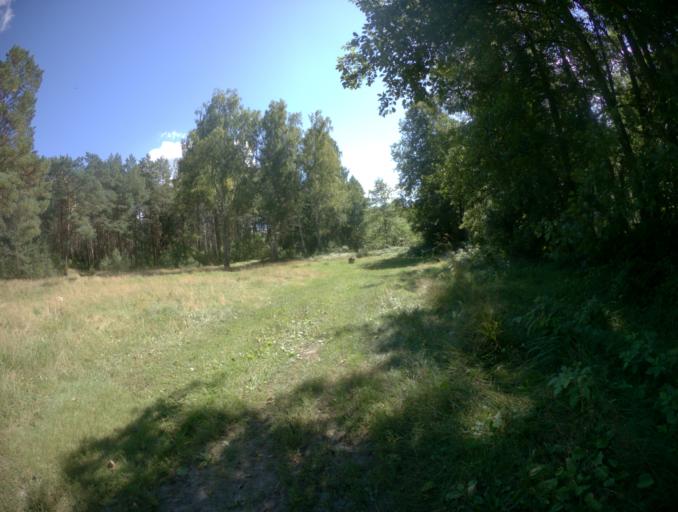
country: RU
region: Vladimir
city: Krasnaya Gorbatka
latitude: 55.8642
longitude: 41.8340
